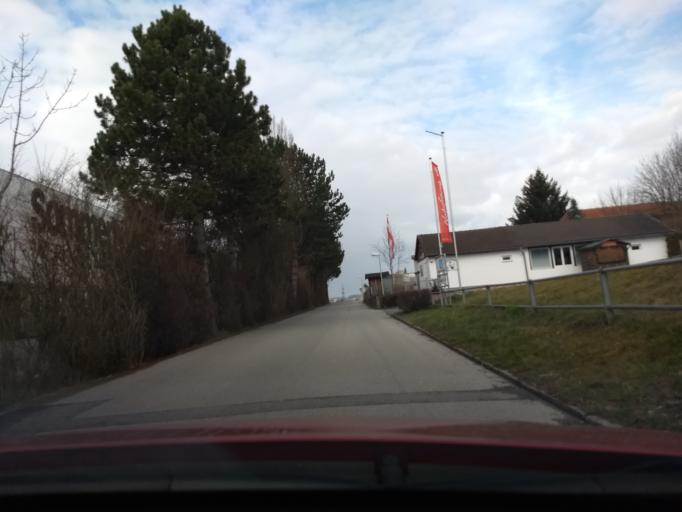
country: AT
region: Upper Austria
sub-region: Steyr Stadt
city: Steyr
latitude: 48.0631
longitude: 14.4240
